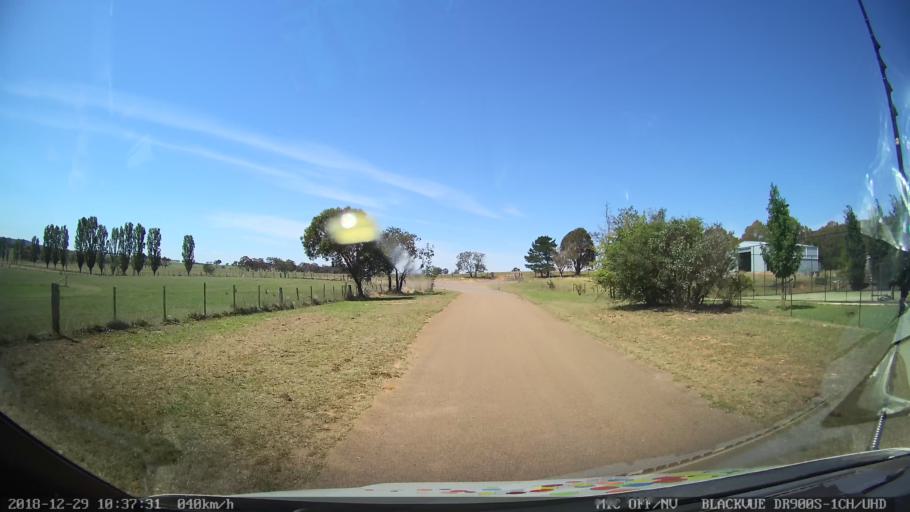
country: AU
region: New South Wales
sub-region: Yass Valley
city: Gundaroo
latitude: -34.9982
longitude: 149.4989
